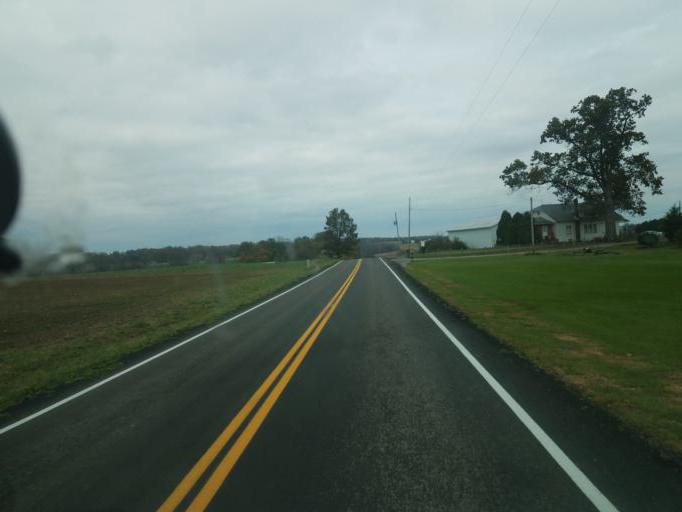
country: US
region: Ohio
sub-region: Wayne County
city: Shreve
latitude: 40.5917
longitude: -82.0636
